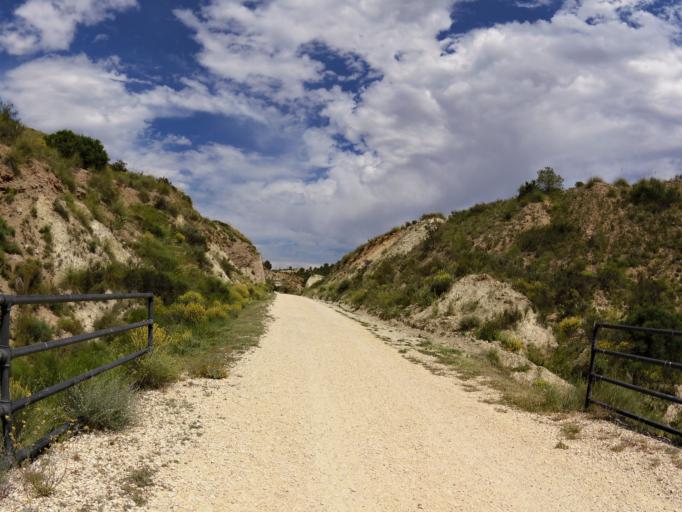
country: ES
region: Valencia
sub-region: Provincia de Alicante
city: Agost
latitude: 38.4831
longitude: -0.6277
